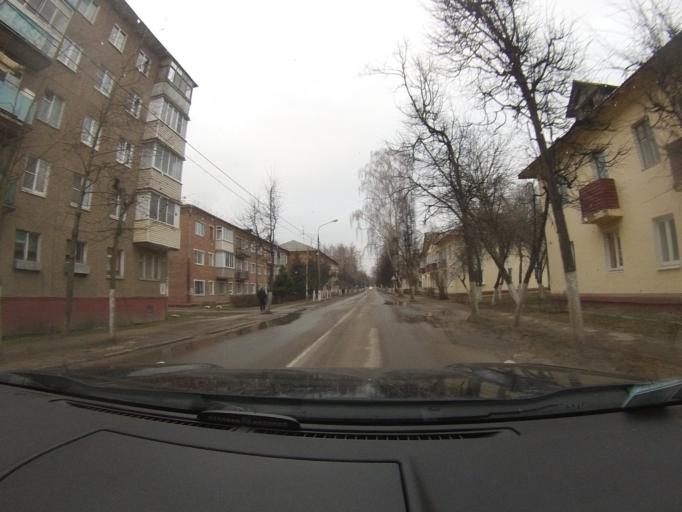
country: RU
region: Moskovskaya
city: Peski
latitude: 55.2473
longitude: 38.7605
